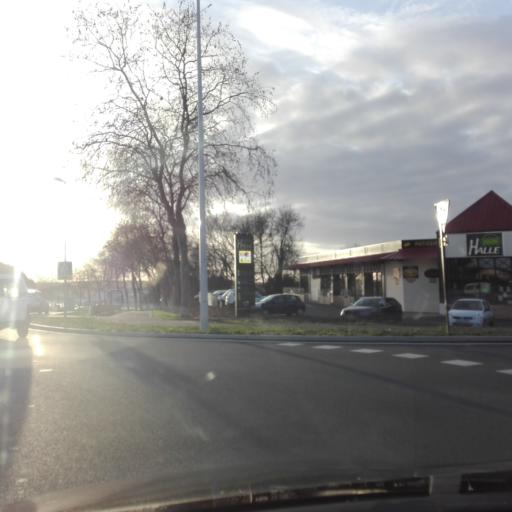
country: FR
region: Pays de la Loire
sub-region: Departement de la Vendee
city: Les Herbiers
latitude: 46.8770
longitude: -1.0217
